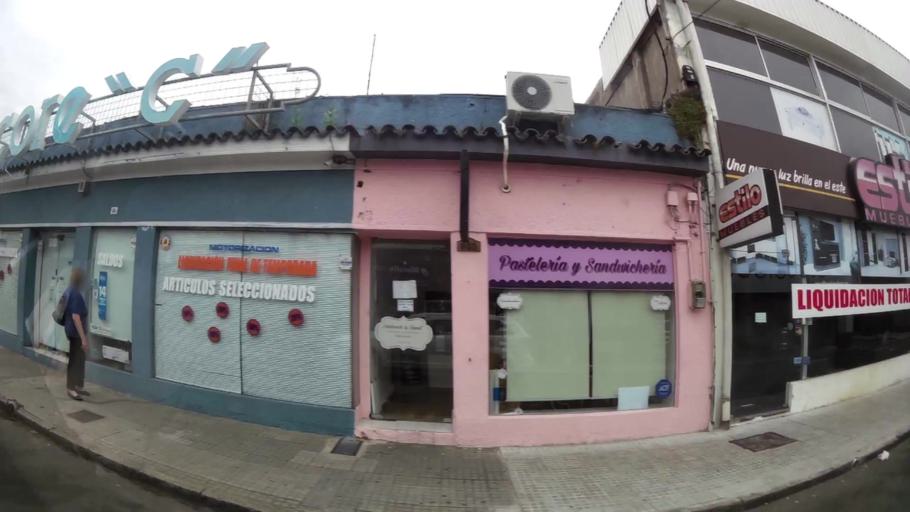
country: UY
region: Maldonado
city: Maldonado
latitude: -34.9067
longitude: -54.9589
